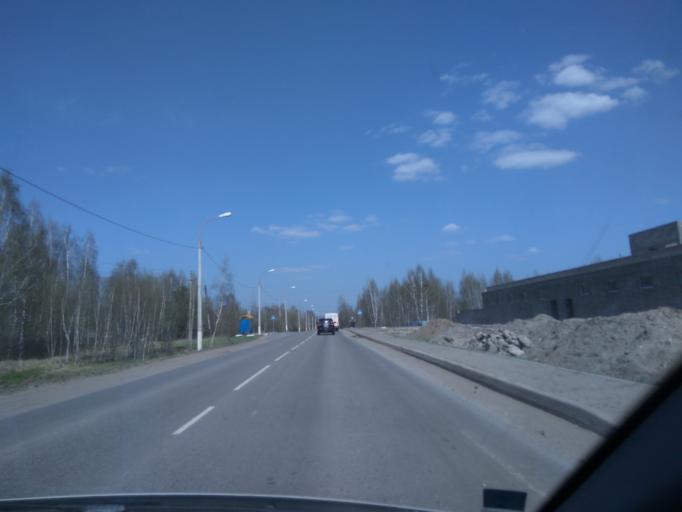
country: RU
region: Moskovskaya
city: Ramenskoye
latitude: 55.5736
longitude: 38.2677
